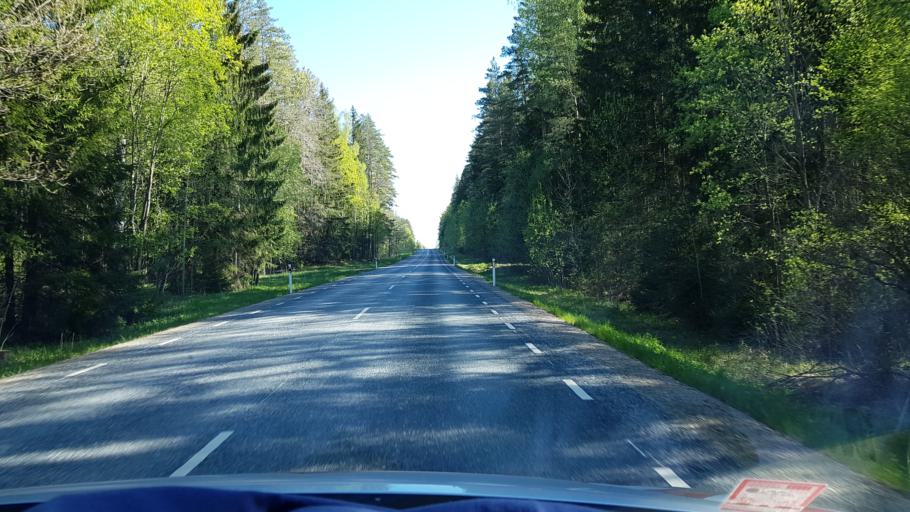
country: EE
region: Polvamaa
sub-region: Polva linn
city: Polva
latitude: 58.1448
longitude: 27.1662
